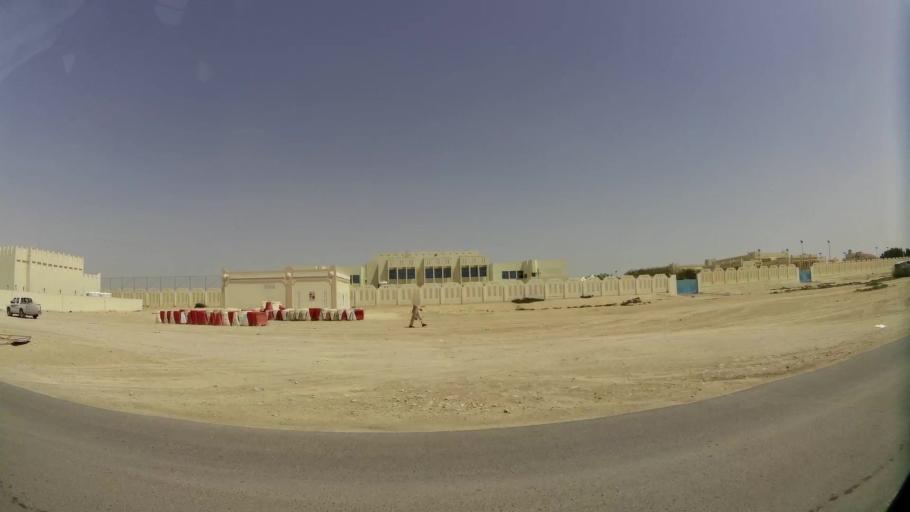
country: QA
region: Baladiyat Umm Salal
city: Umm Salal Muhammad
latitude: 25.3955
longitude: 51.4449
